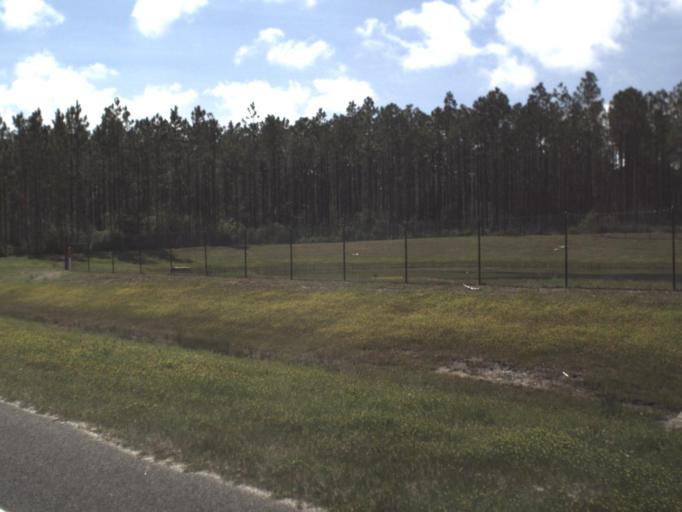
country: US
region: Florida
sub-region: Bay County
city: Laguna Beach
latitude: 30.3577
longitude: -85.8590
